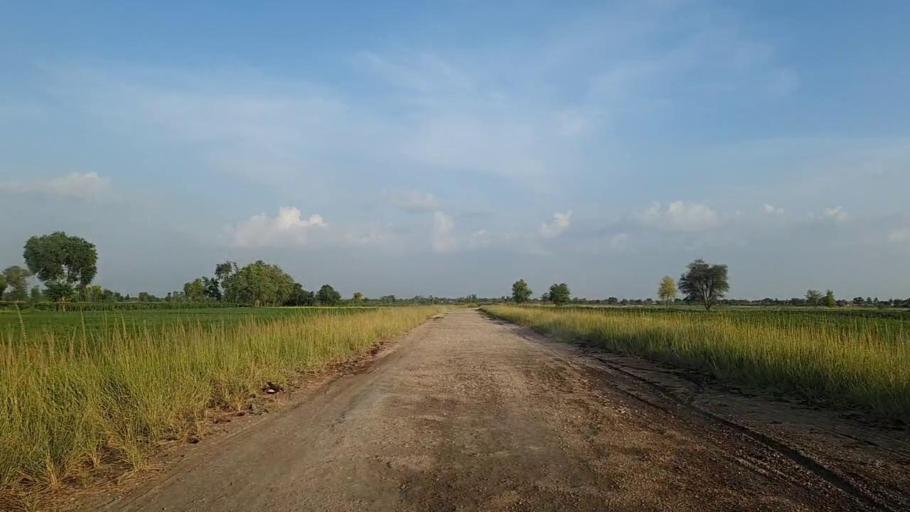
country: PK
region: Sindh
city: Karaundi
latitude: 27.0536
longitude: 68.4034
